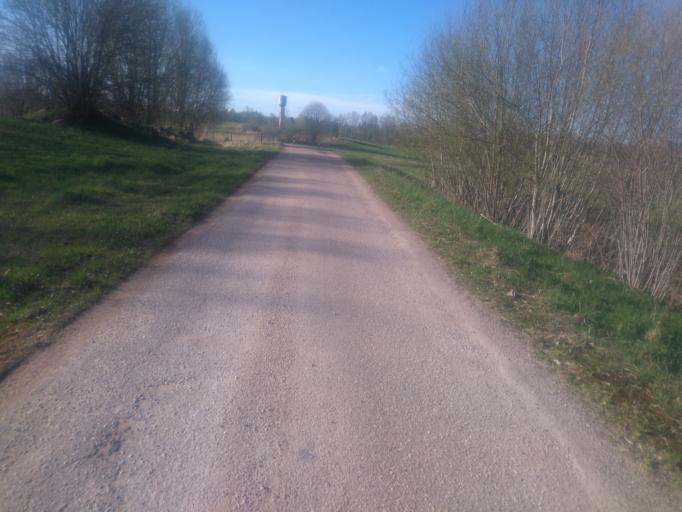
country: LV
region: Vecpiebalga
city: Vecpiebalga
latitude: 57.0198
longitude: 25.8519
